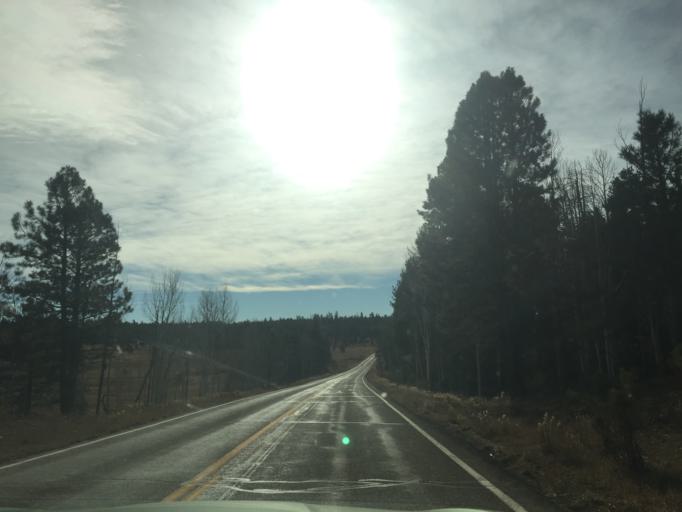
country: US
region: Utah
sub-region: Garfield County
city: Panguitch
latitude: 37.5084
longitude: -112.6286
